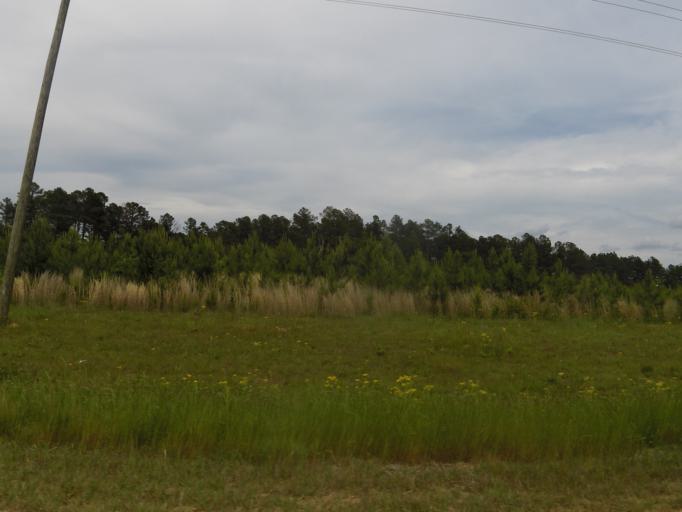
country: US
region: Georgia
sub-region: Jefferson County
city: Wrens
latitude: 33.3095
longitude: -82.4453
